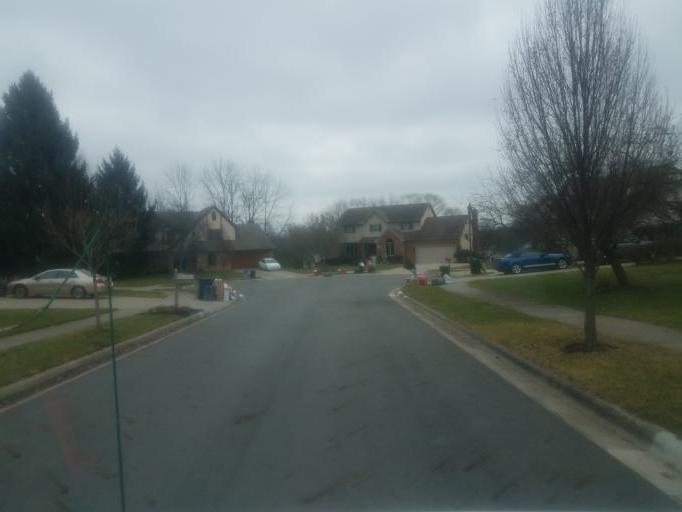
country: US
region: Ohio
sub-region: Franklin County
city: Westerville
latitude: 40.1299
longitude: -82.9519
